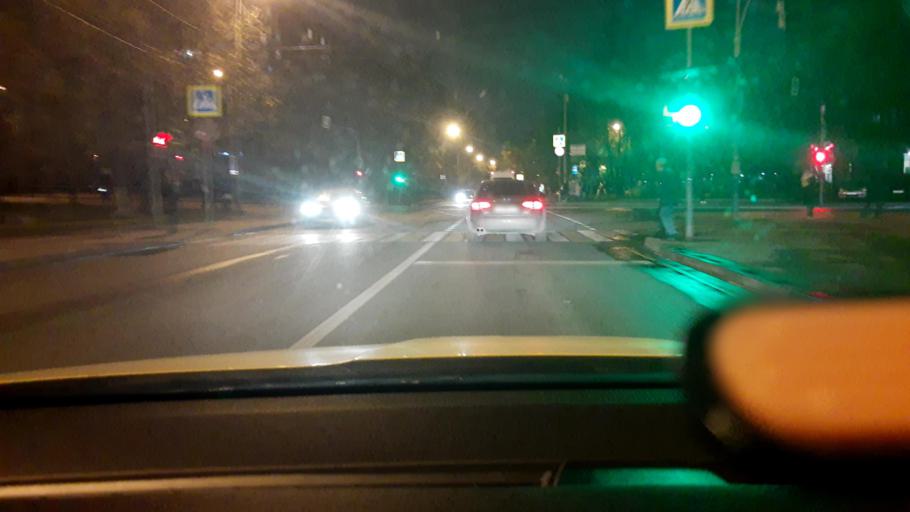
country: RU
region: Moscow
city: Tekstil'shchiki
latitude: 55.6858
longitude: 37.7237
